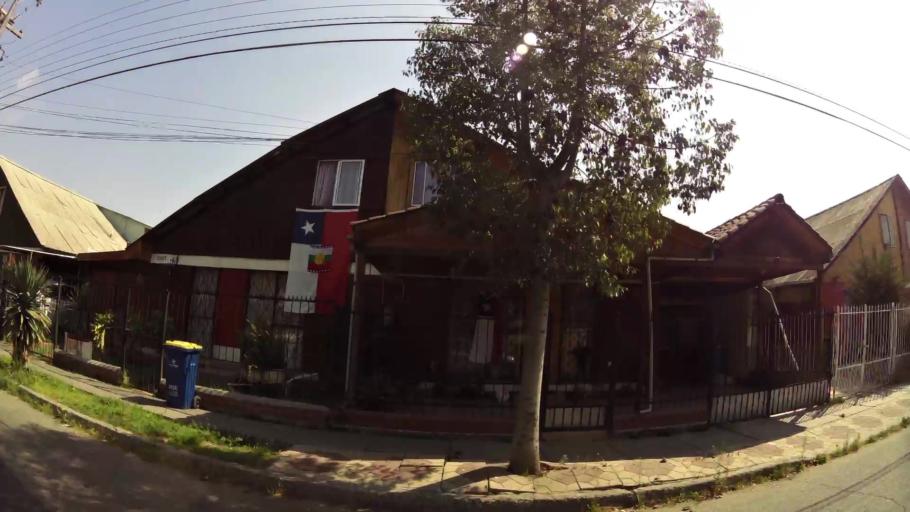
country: CL
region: Santiago Metropolitan
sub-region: Provincia de Santiago
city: La Pintana
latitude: -33.5491
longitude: -70.6003
